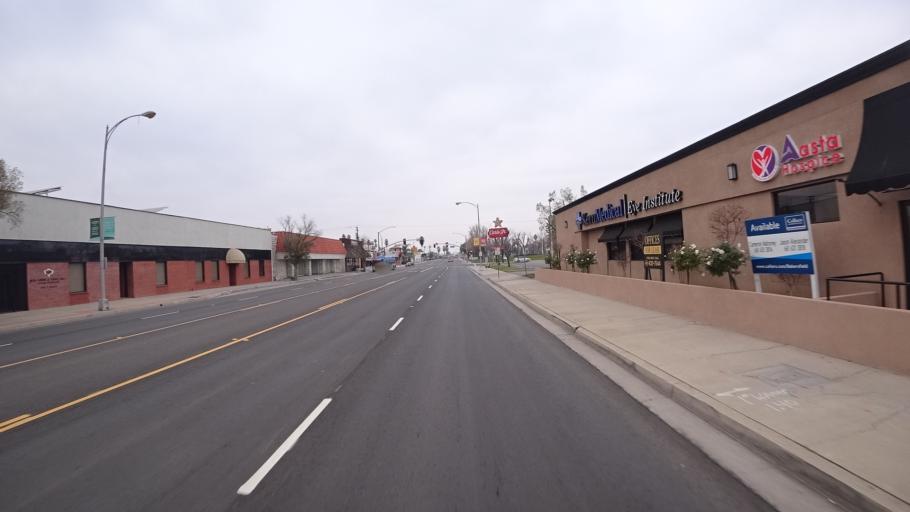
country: US
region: California
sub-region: Kern County
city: Bakersfield
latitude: 35.3859
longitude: -119.0234
